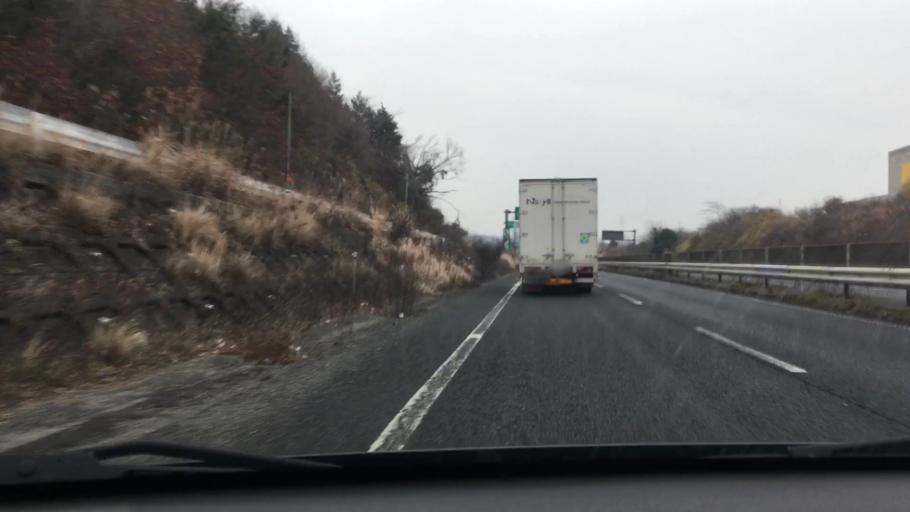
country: JP
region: Mie
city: Ueno-ebisumachi
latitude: 34.7116
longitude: 136.0785
